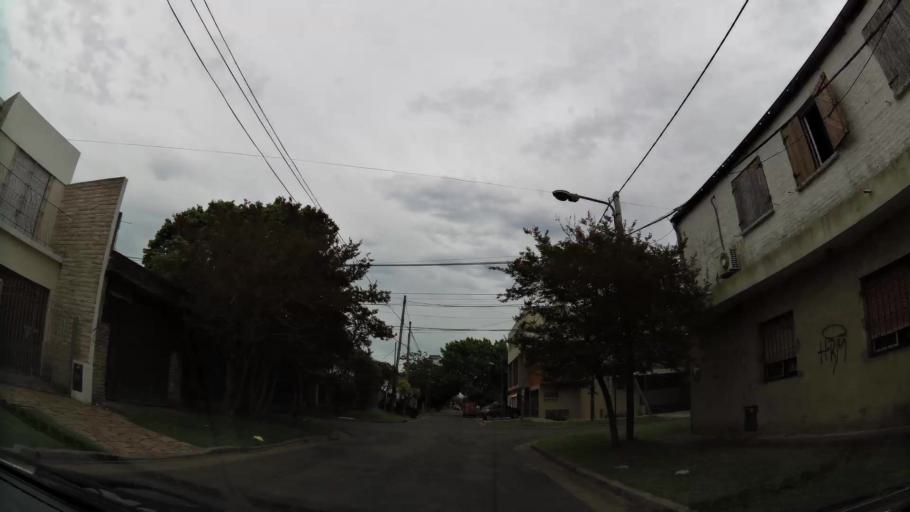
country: AR
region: Buenos Aires
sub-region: Partido de Quilmes
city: Quilmes
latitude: -34.7528
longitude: -58.2095
